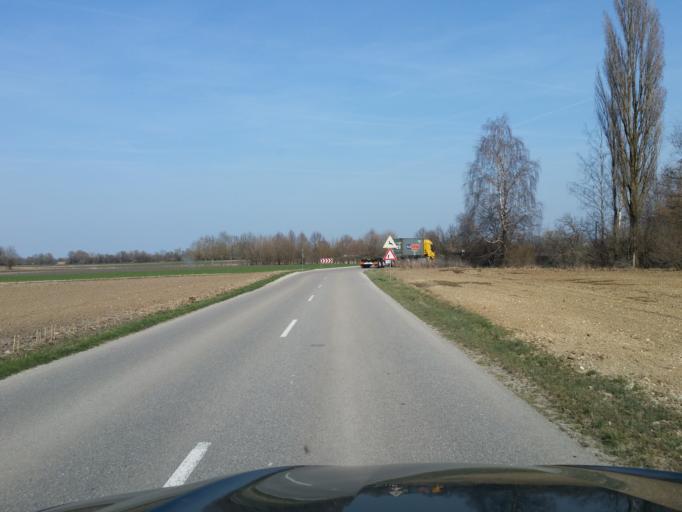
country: DE
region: Bavaria
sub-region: Upper Bavaria
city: Eitting
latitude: 48.3959
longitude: 11.9025
